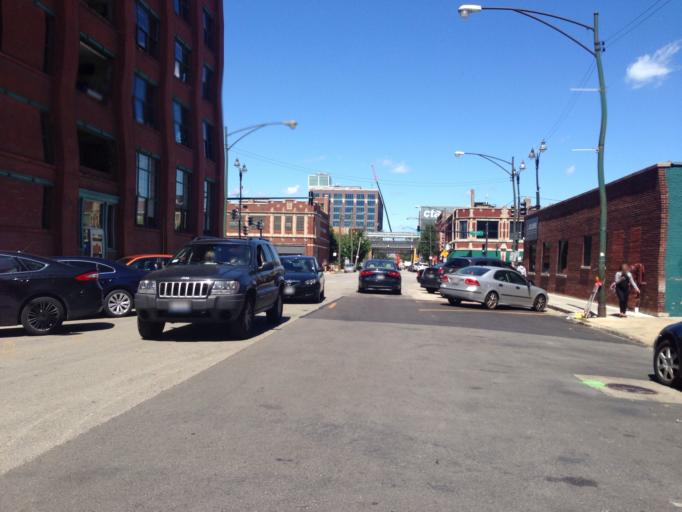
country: US
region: Illinois
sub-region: Cook County
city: Chicago
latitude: 41.8834
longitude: -87.6522
